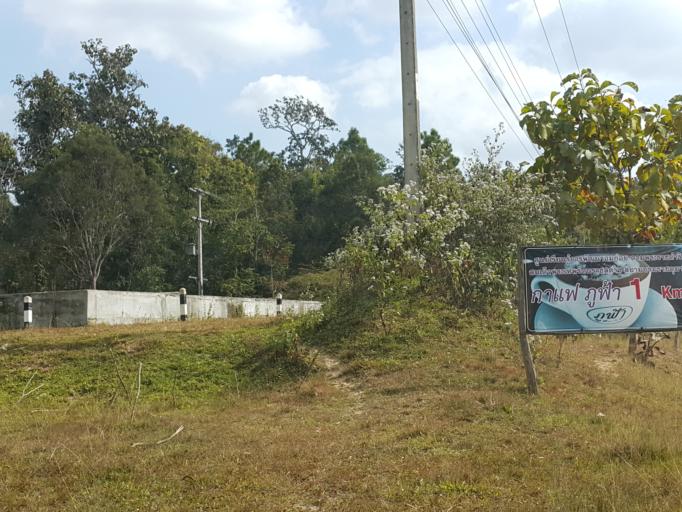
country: TH
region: Chiang Mai
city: Om Koi
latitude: 17.8461
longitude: 98.3714
